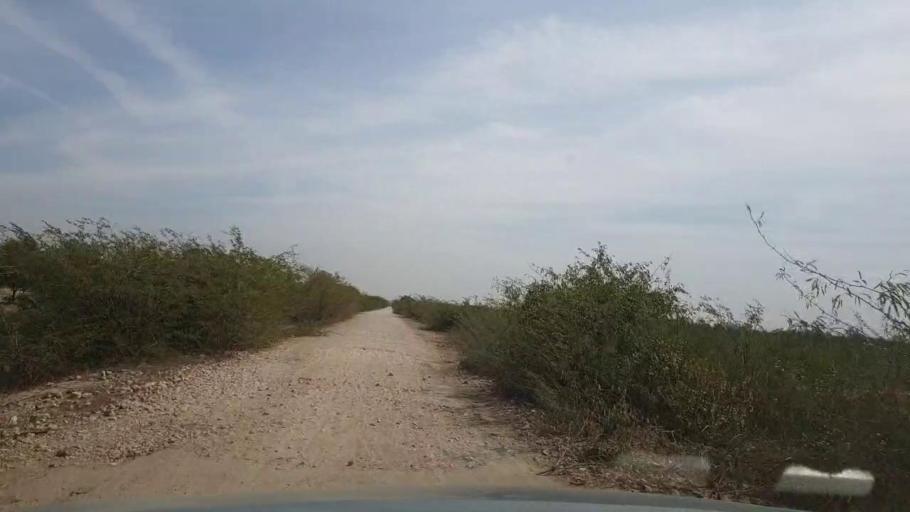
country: PK
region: Sindh
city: Nabisar
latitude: 25.1189
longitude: 69.6201
